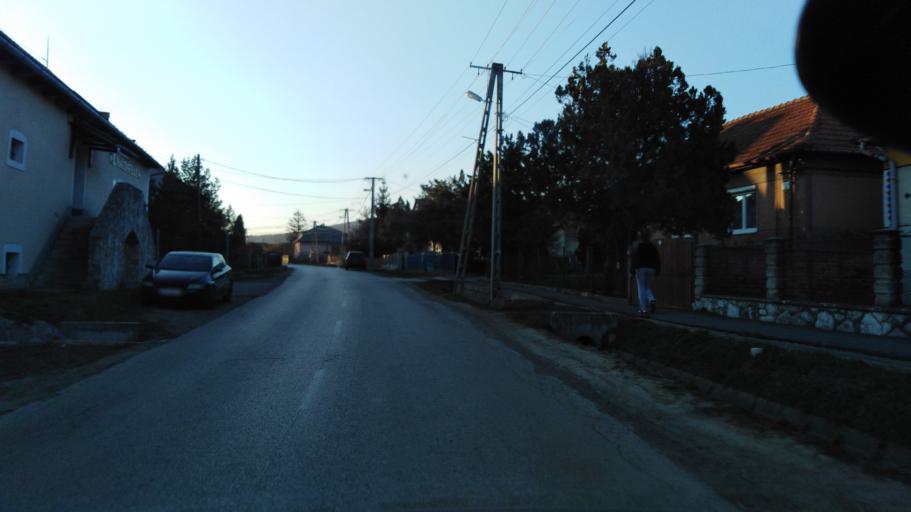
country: HU
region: Nograd
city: Kazar
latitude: 48.0481
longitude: 19.8639
